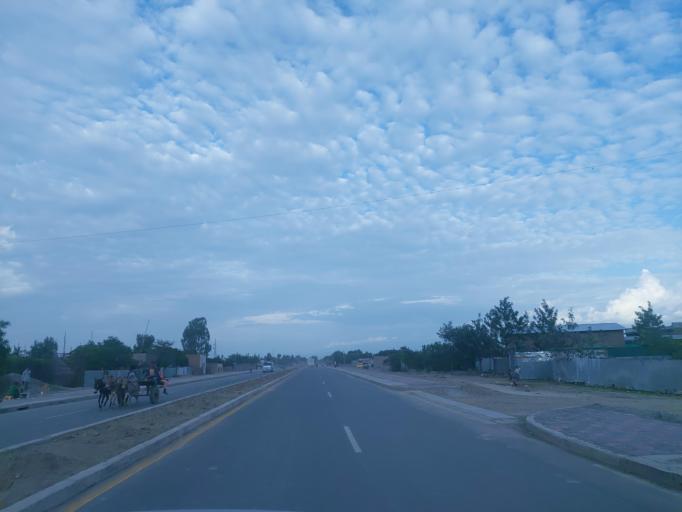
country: ET
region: Oromiya
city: Ziway
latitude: 8.1466
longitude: 38.8032
